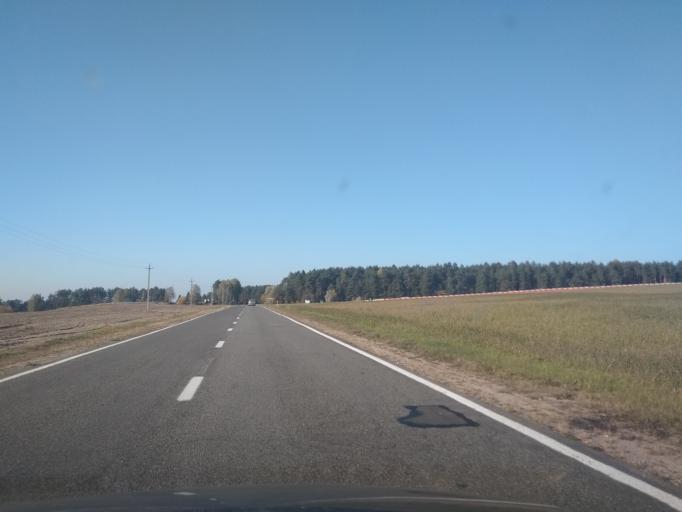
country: BY
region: Grodnenskaya
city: Vawkavysk
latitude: 53.1488
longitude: 24.5013
